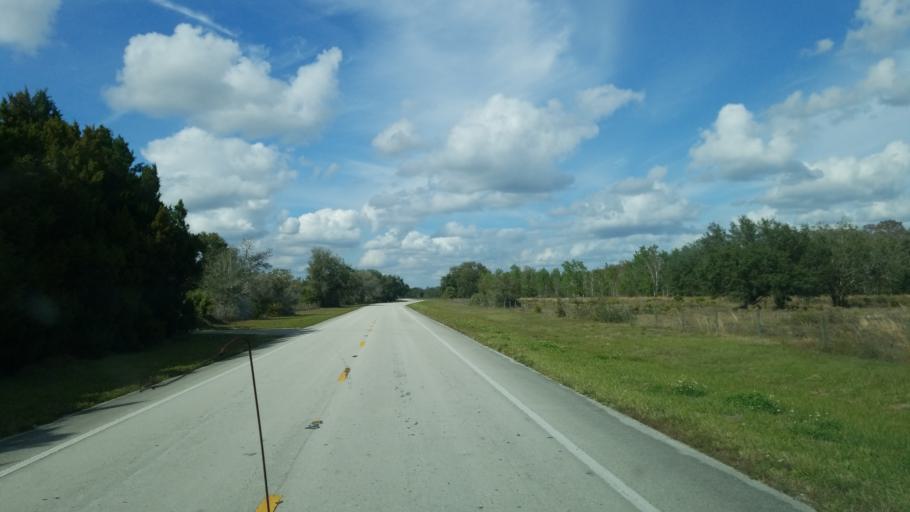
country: US
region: Florida
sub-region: Brevard County
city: June Park
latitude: 27.9513
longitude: -80.9997
